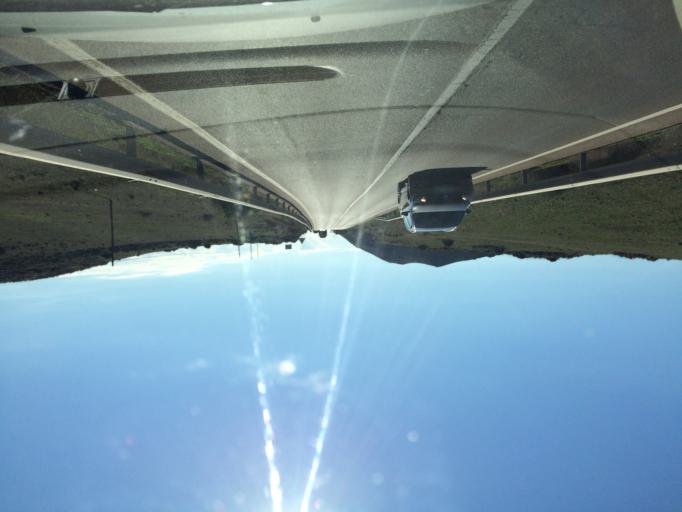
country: ES
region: Andalusia
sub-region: Provincia de Almeria
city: San Jose
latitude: 36.7834
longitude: -2.1084
